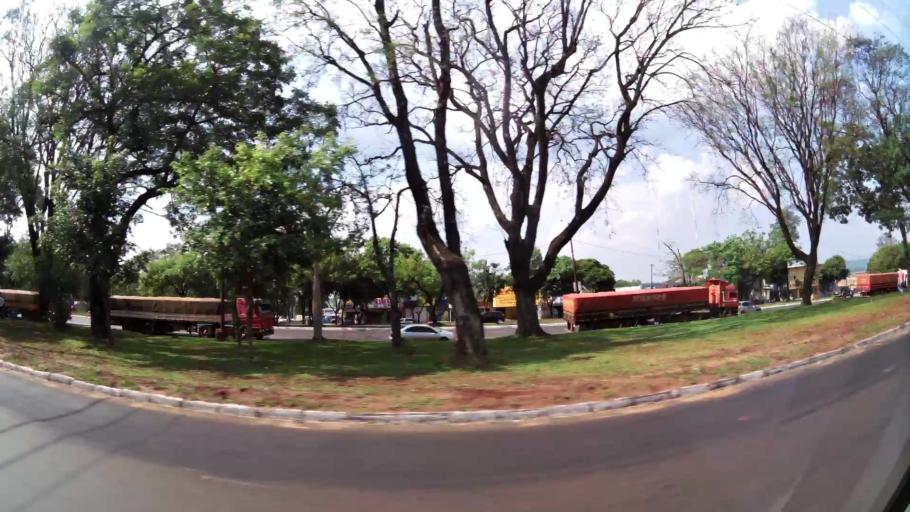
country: PY
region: Alto Parana
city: Ciudad del Este
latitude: -25.5089
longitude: -54.6338
